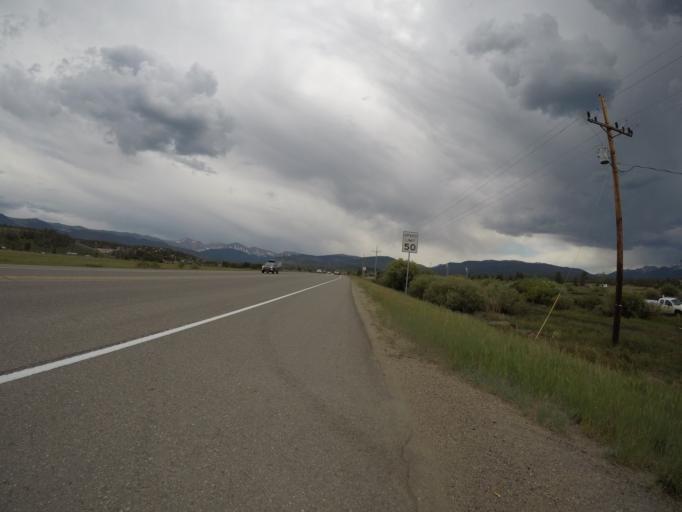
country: US
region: Colorado
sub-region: Grand County
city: Fraser
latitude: 39.9570
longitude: -105.8204
